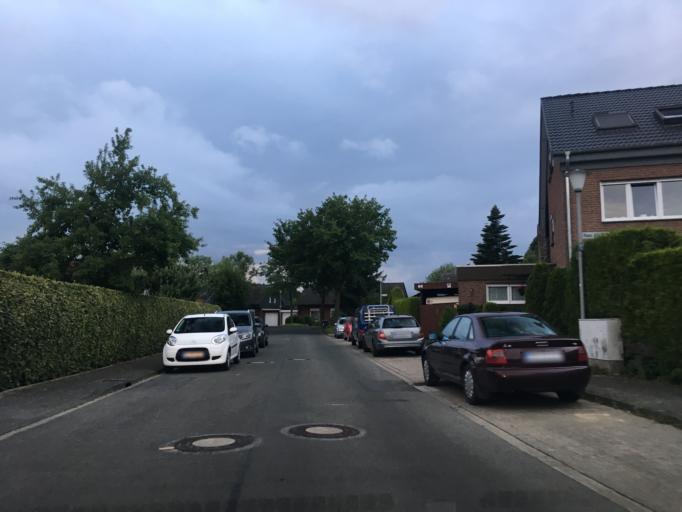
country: DE
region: North Rhine-Westphalia
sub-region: Regierungsbezirk Munster
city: Muenster
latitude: 51.9479
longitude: 7.6694
